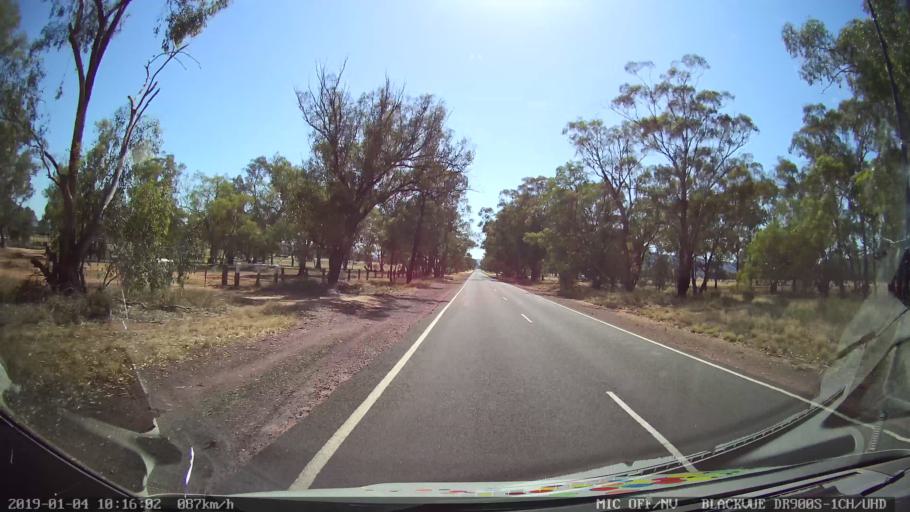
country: AU
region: New South Wales
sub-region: Cabonne
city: Canowindra
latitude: -33.3861
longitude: 148.4304
